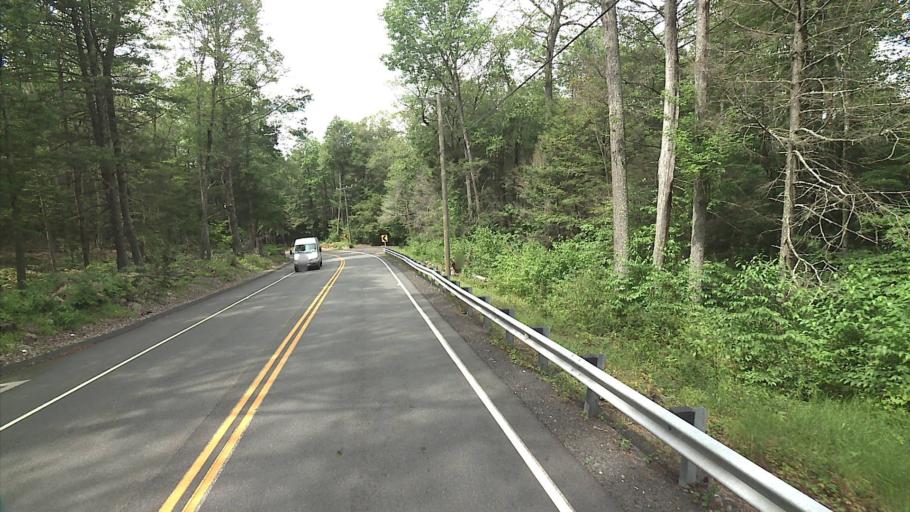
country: US
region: Massachusetts
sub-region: Hampden County
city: Holland
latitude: 41.9904
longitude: -72.1248
